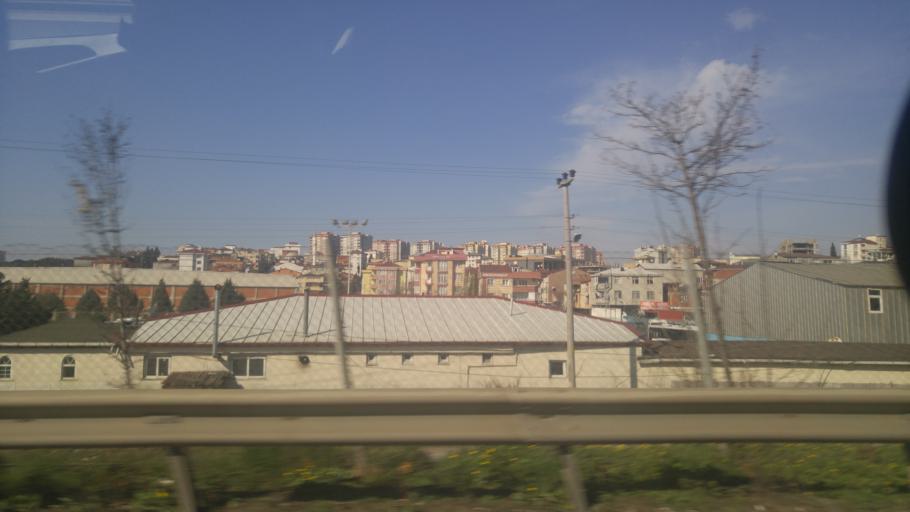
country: TR
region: Kocaeli
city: Darica
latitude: 40.8268
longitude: 29.3653
